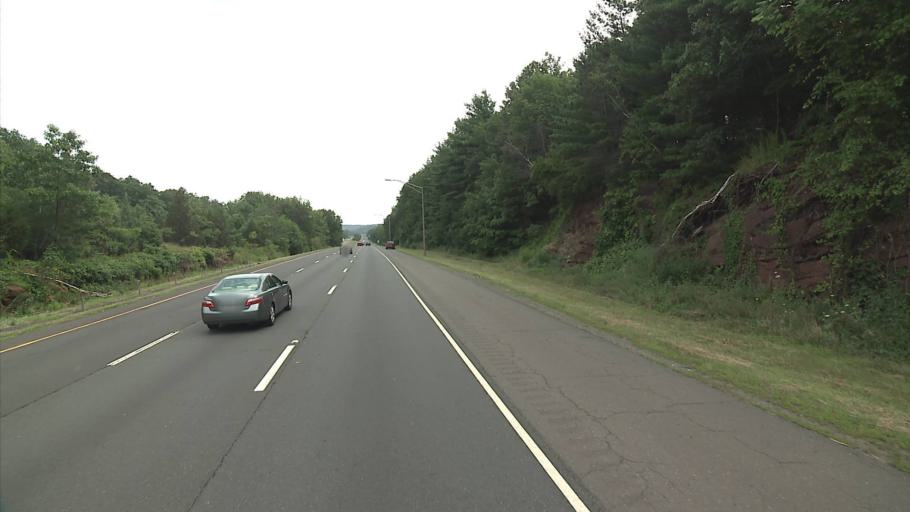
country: US
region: Connecticut
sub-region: Hartford County
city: Plainville
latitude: 41.6379
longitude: -72.8669
